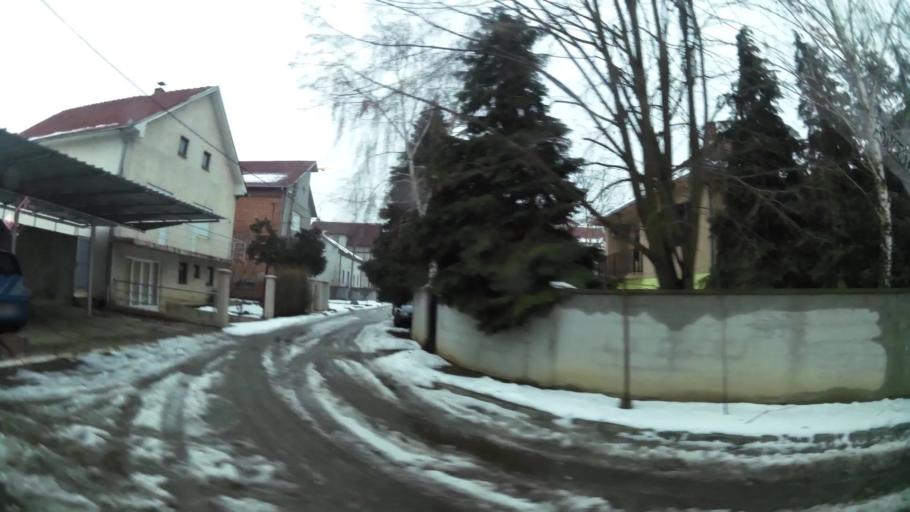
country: RS
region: Central Serbia
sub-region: Belgrade
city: Zemun
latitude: 44.8120
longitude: 20.3718
